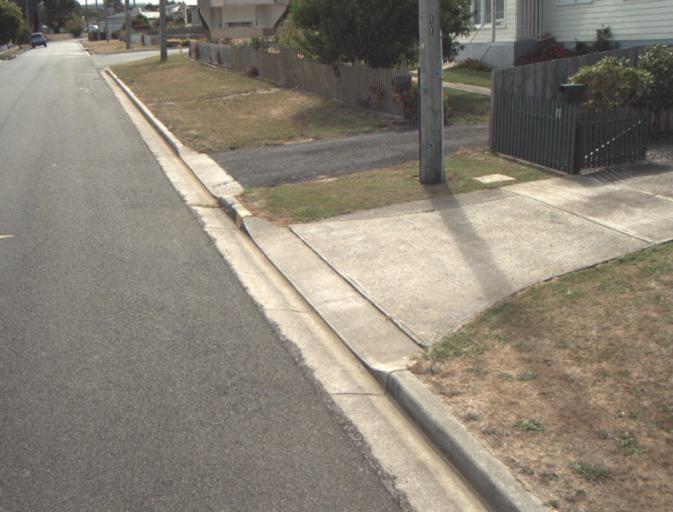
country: AU
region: Tasmania
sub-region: Launceston
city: Mayfield
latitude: -41.3829
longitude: 147.1265
